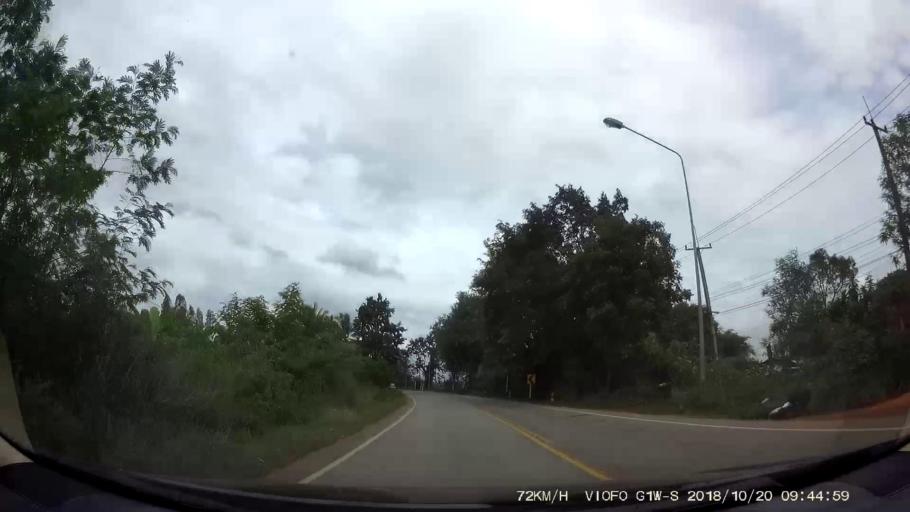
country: TH
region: Chaiyaphum
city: Khon San
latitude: 16.4886
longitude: 101.9411
